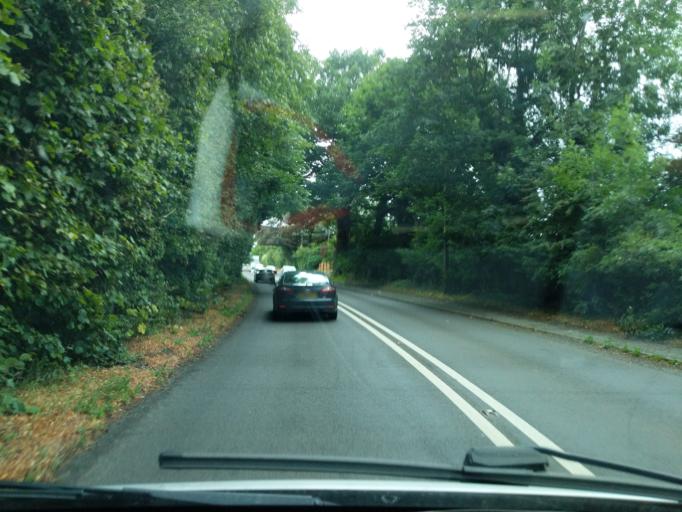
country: GB
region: England
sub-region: Cheshire West and Chester
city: Cuddington
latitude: 53.2376
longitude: -2.6026
